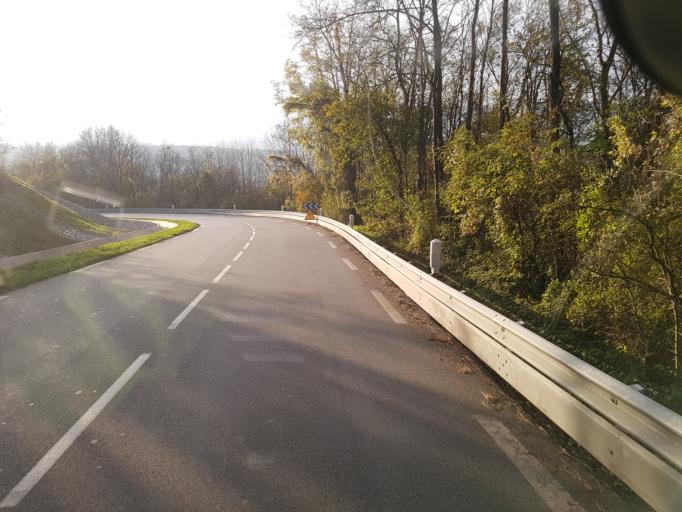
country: FR
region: Rhone-Alpes
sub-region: Departement de l'Ain
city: Bellegarde-sur-Valserine
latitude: 46.1046
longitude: 5.8303
